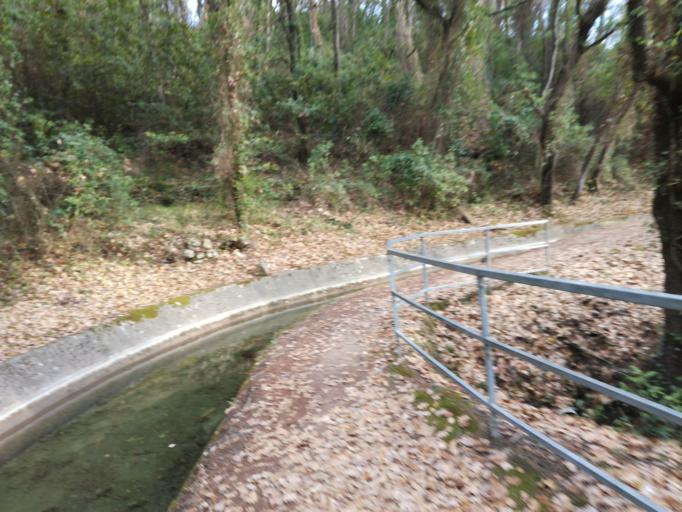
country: FR
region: Provence-Alpes-Cote d'Azur
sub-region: Departement des Alpes-Maritimes
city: Mouans-Sartoux
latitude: 43.6255
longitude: 6.9803
